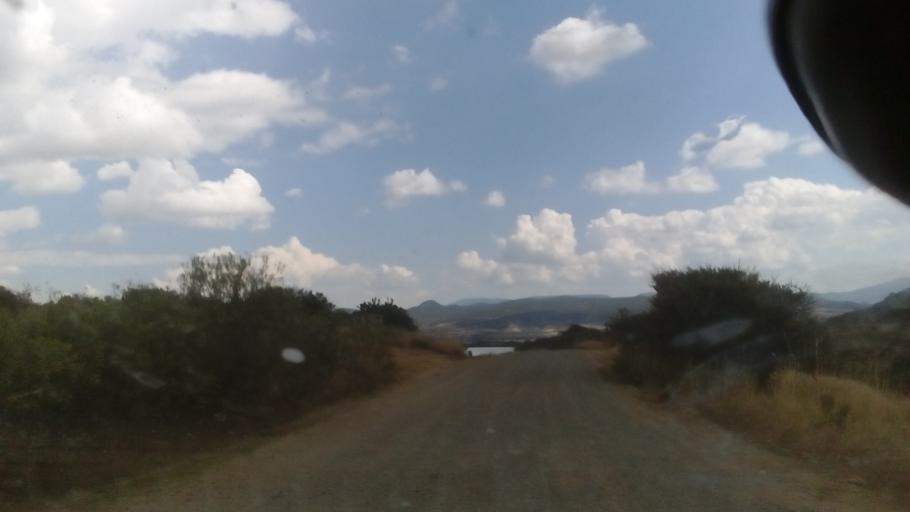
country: MX
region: Guanajuato
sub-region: Silao de la Victoria
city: San Francisco (Banos de Agua Caliente)
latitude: 21.1946
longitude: -101.4583
